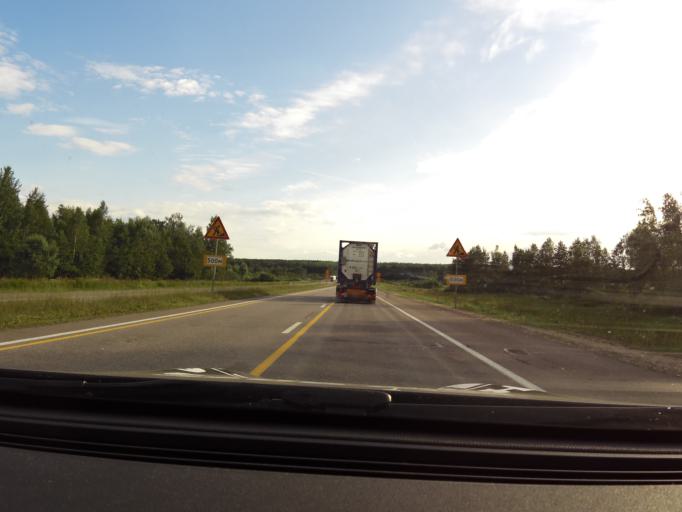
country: RU
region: Vladimir
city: Sudogda
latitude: 56.1282
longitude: 40.8722
